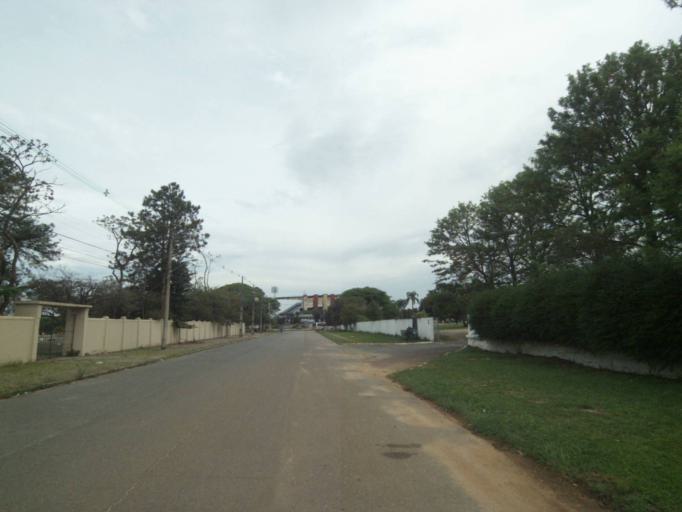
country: BR
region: Parana
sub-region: Pinhais
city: Pinhais
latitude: -25.4281
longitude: -49.2217
